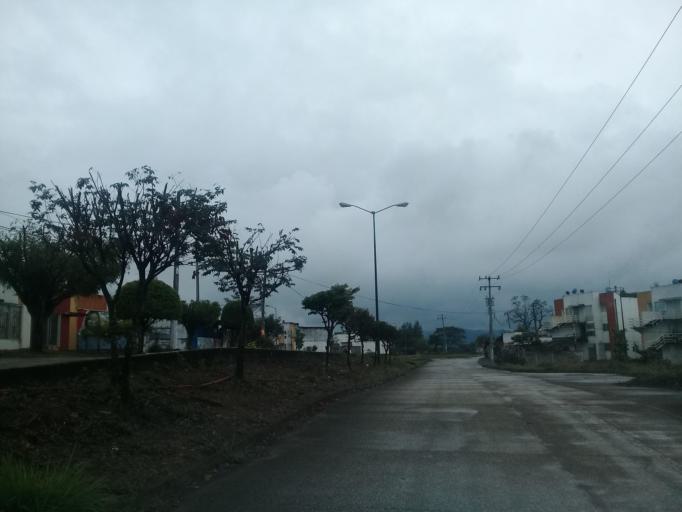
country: MX
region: Veracruz
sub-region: Amatlan de los Reyes
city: Trapiche Viejo
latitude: 18.8369
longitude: -96.9535
